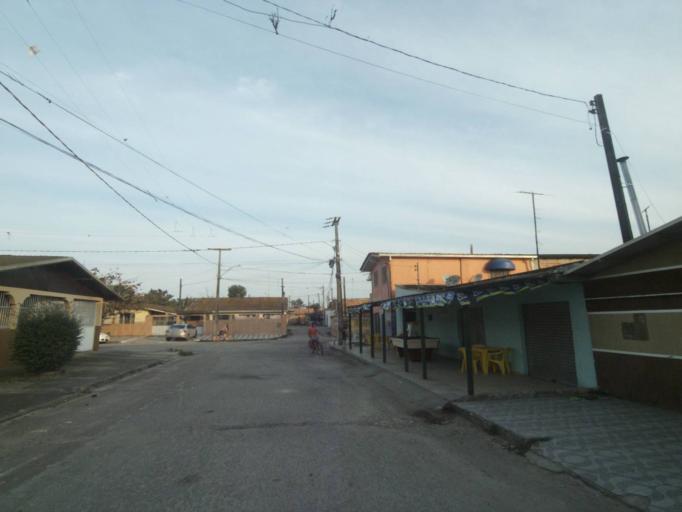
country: BR
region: Parana
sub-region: Paranagua
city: Paranagua
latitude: -25.5189
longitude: -48.5449
